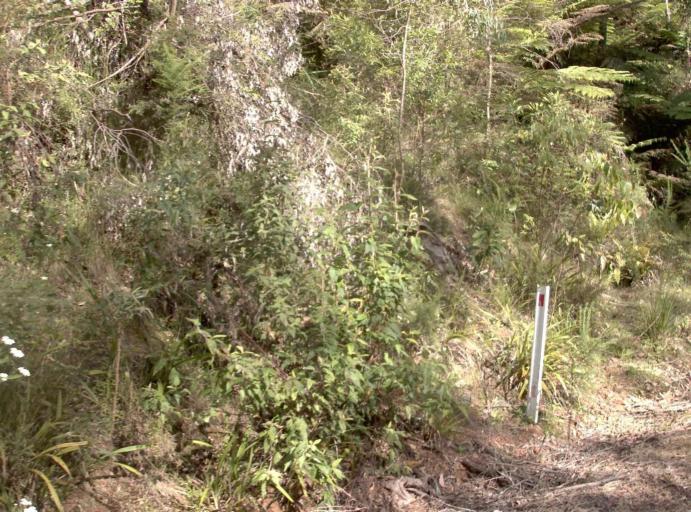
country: AU
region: Victoria
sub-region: East Gippsland
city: Lakes Entrance
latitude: -37.4059
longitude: 148.5927
